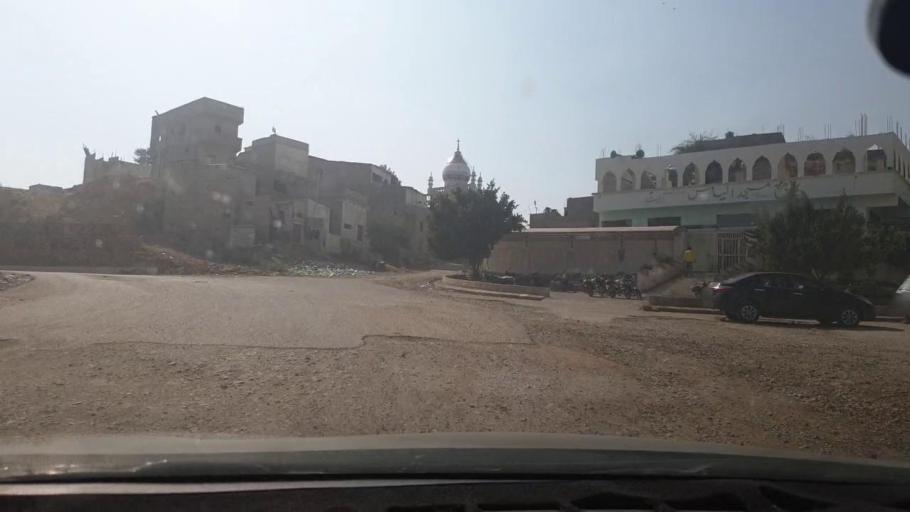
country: PK
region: Sindh
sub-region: Karachi District
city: Karachi
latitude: 24.9736
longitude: 66.9982
